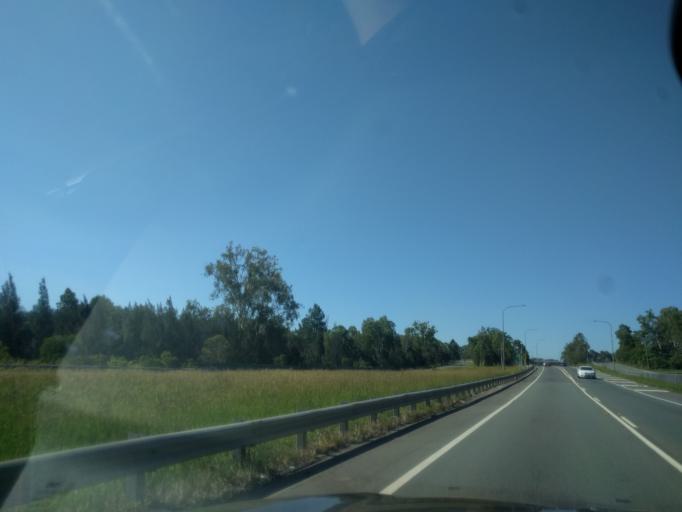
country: AU
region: Queensland
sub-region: Logan
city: Park Ridge South
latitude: -27.7304
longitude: 153.0291
